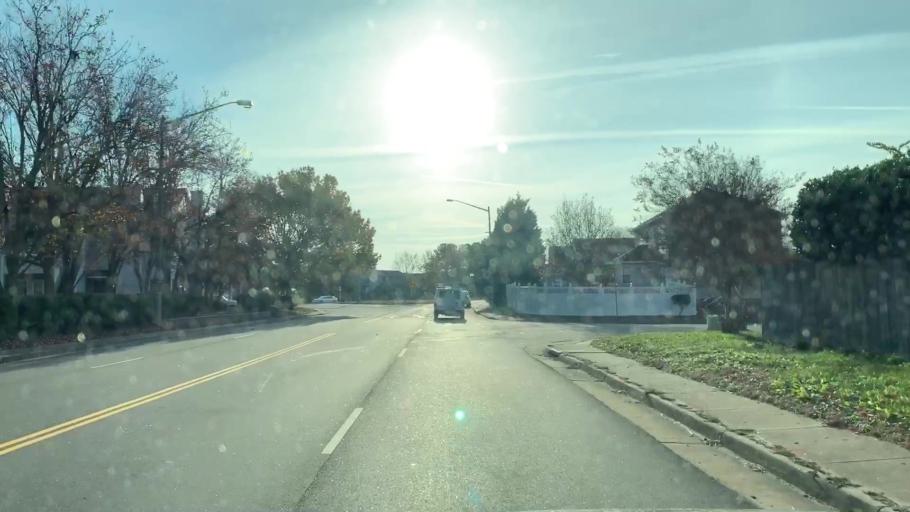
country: US
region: Virginia
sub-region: City of Chesapeake
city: Chesapeake
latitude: 36.7902
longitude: -76.1653
